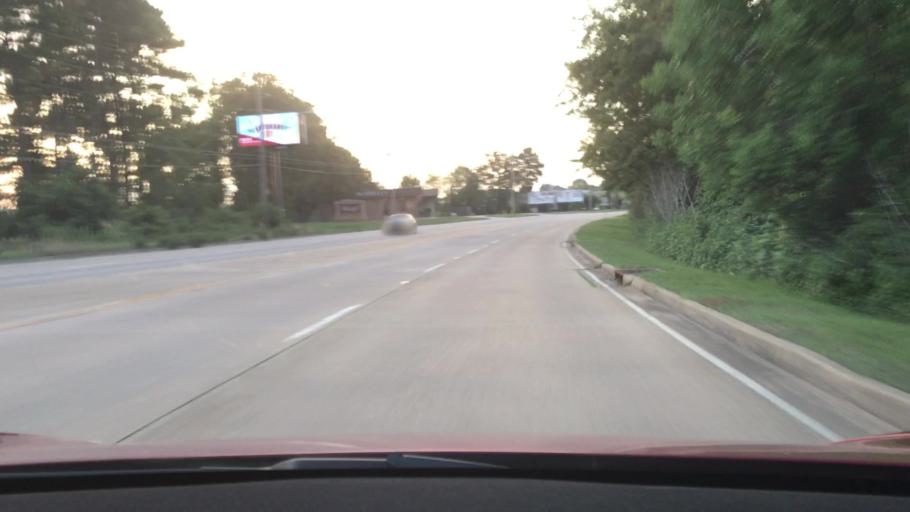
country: US
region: Louisiana
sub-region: Bossier Parish
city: Bossier City
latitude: 32.4055
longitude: -93.7380
